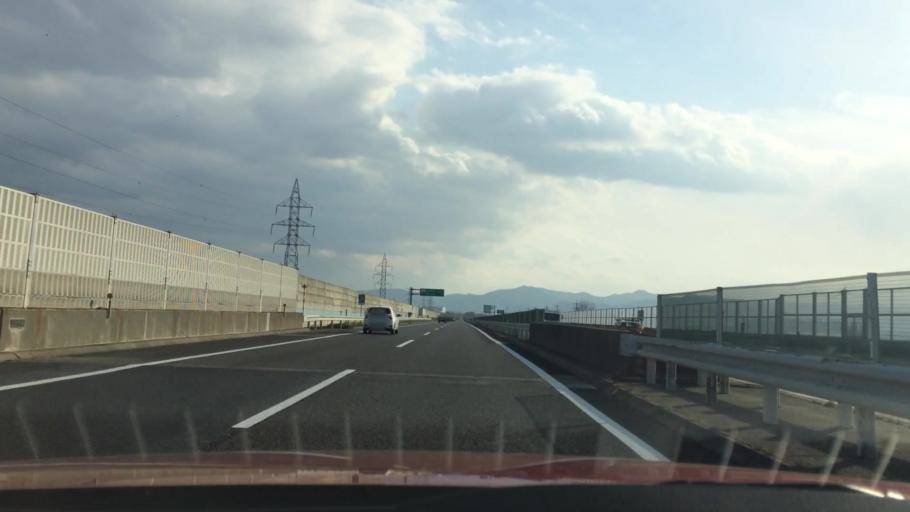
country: JP
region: Nagano
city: Matsumoto
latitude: 36.1864
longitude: 137.9381
